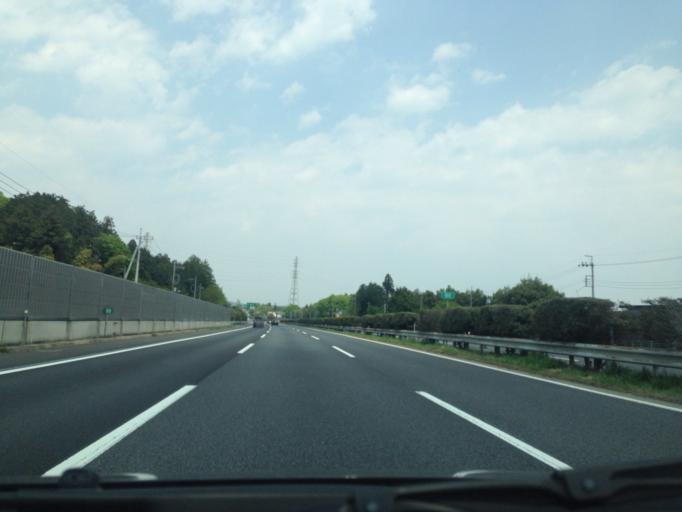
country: JP
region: Tochigi
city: Utsunomiya-shi
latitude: 36.5876
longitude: 139.8383
